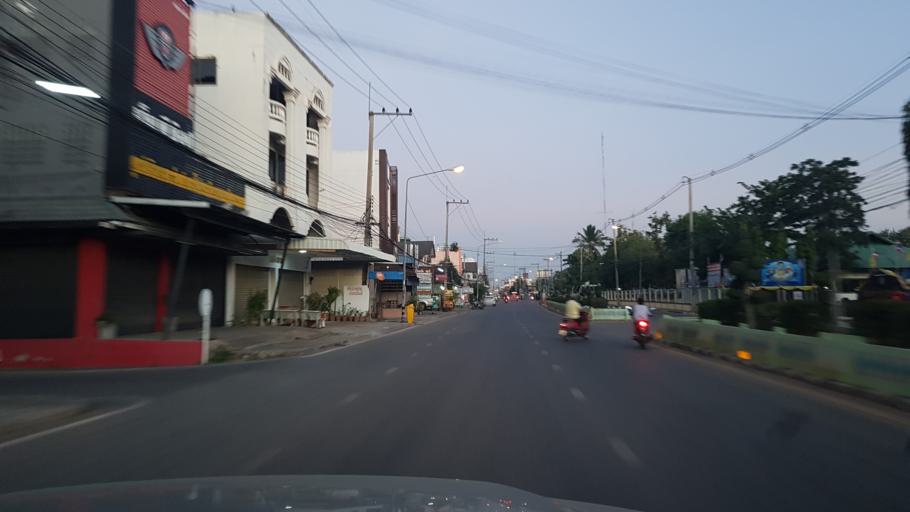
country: TH
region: Chaiyaphum
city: Phu Khiao
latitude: 16.3670
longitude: 102.1310
